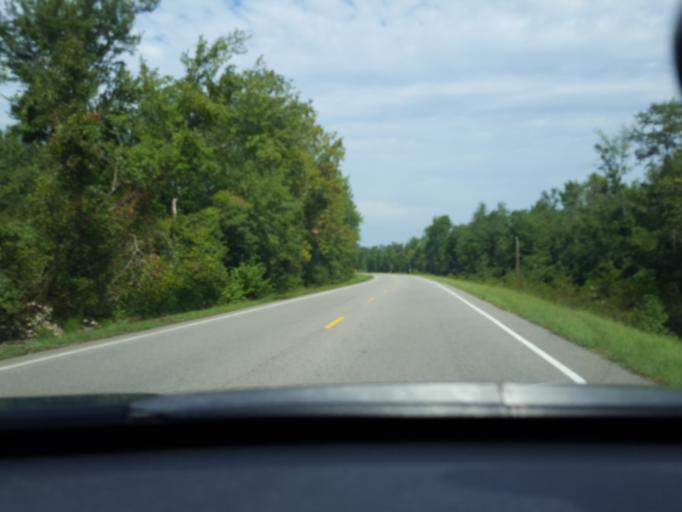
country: US
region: North Carolina
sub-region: Washington County
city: Plymouth
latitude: 35.9081
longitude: -76.7155
